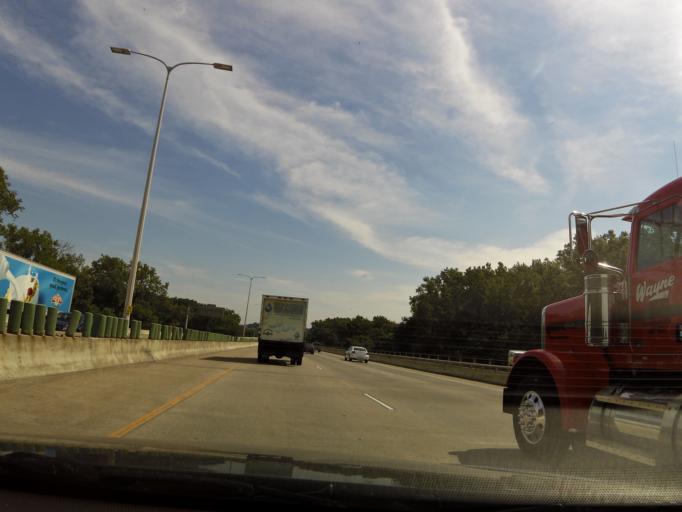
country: US
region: Minnesota
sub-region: Dakota County
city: Mendota Heights
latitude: 44.8620
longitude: -93.2012
